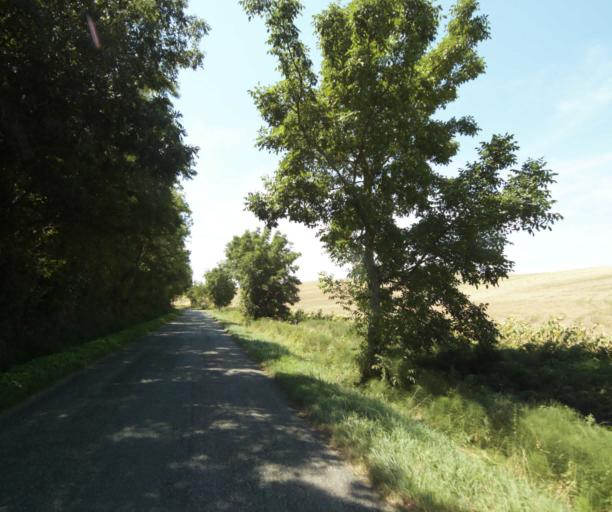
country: FR
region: Midi-Pyrenees
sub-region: Departement de l'Ariege
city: Lezat-sur-Leze
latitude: 43.2619
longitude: 1.3254
